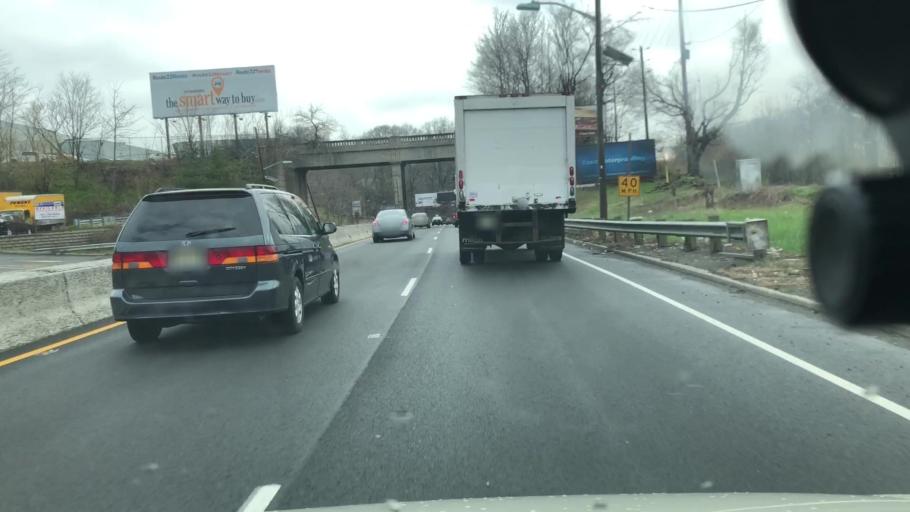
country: US
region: New Jersey
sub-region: Union County
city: Hillside
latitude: 40.6979
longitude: -74.2151
